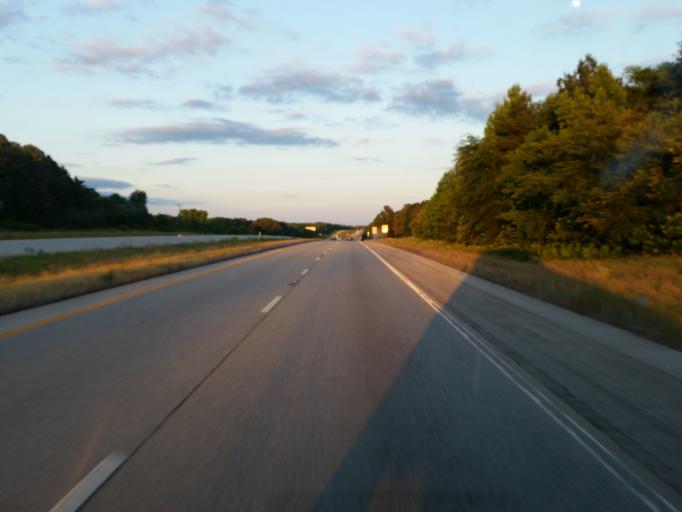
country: US
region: Texas
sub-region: Van Zandt County
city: Van
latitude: 32.4970
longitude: -95.5766
